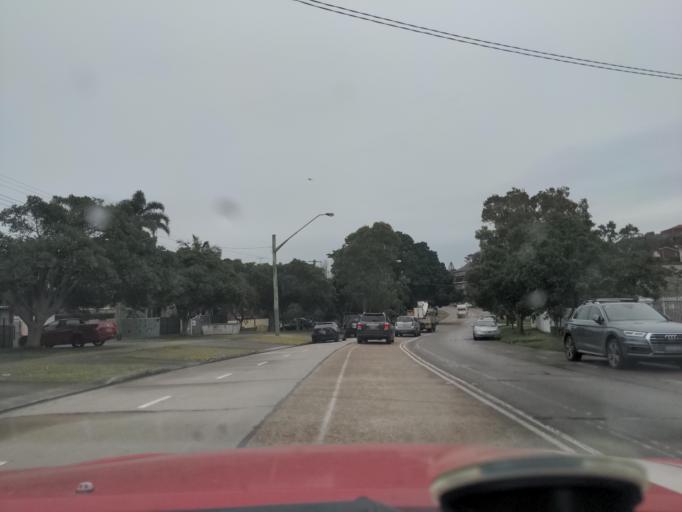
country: AU
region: New South Wales
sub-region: Randwick
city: Maroubra
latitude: -33.9469
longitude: 151.2482
